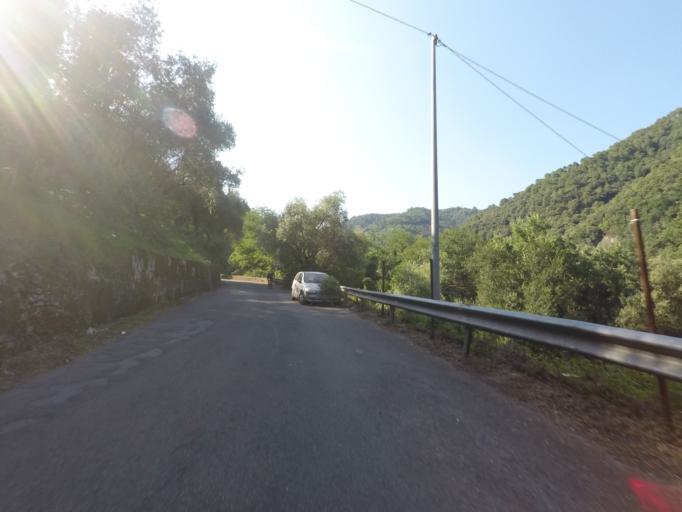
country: IT
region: Tuscany
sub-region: Provincia di Massa-Carrara
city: Carrara
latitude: 44.0785
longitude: 10.0733
